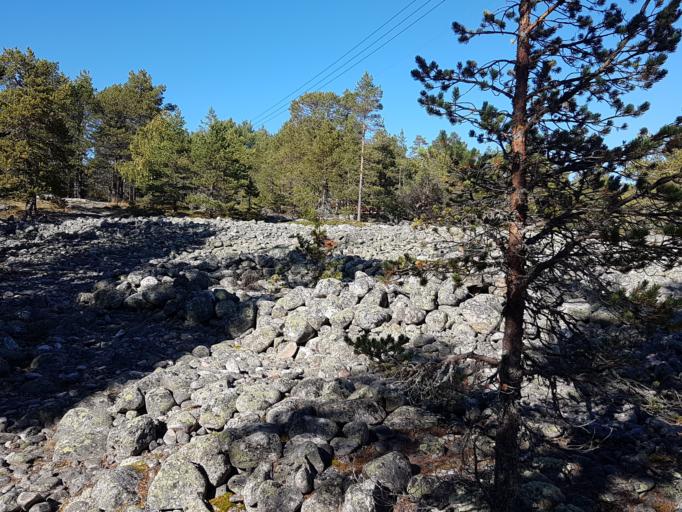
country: SE
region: Vaesterbotten
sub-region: Skelleftea Kommun
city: Skelleftehamn
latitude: 64.4785
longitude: 21.5760
